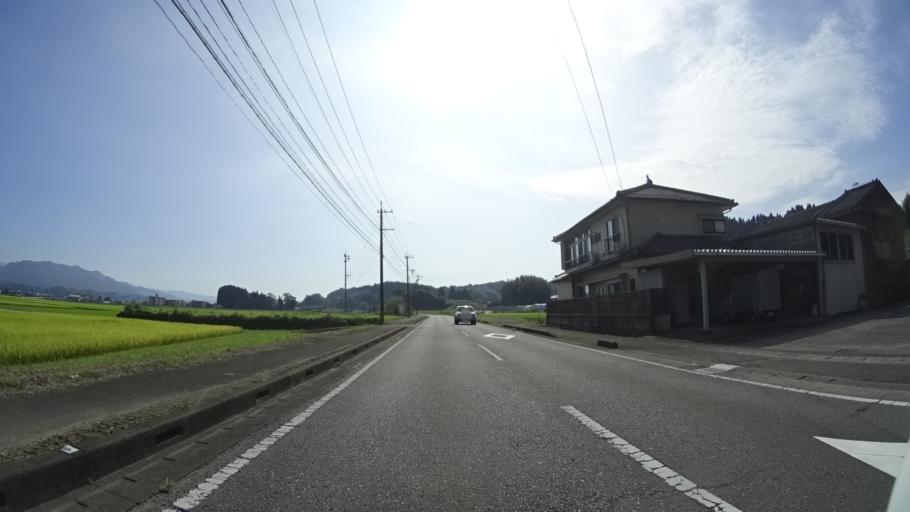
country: JP
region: Kagoshima
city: Okuchi-shinohara
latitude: 32.0377
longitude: 130.8065
